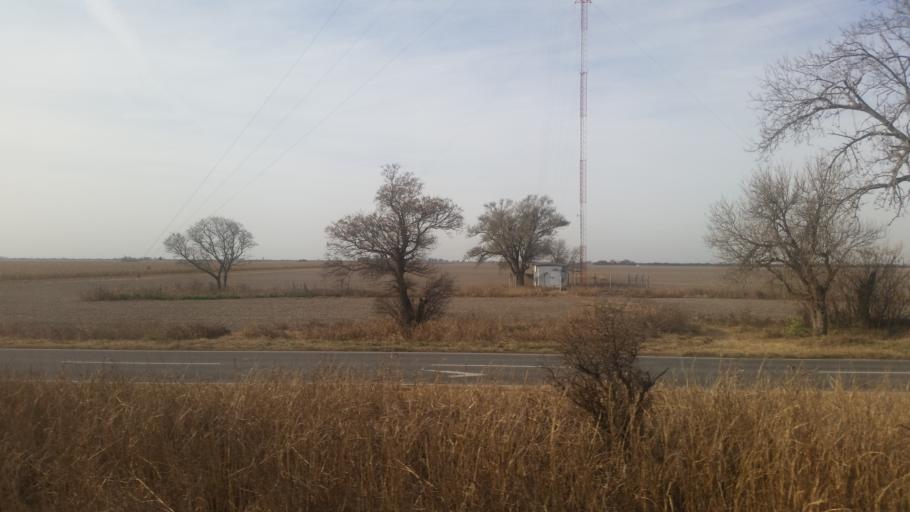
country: AR
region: Cordoba
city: Pilar
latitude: -31.7304
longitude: -63.8437
